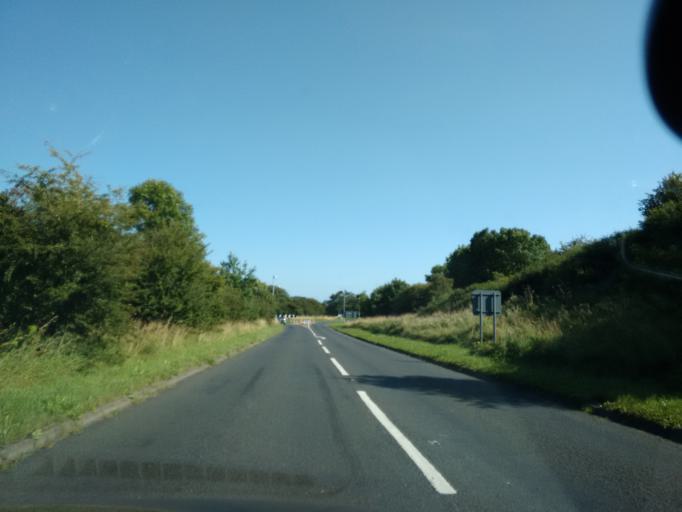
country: GB
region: England
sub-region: Northumberland
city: Corbridge
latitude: 55.0133
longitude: -2.0239
